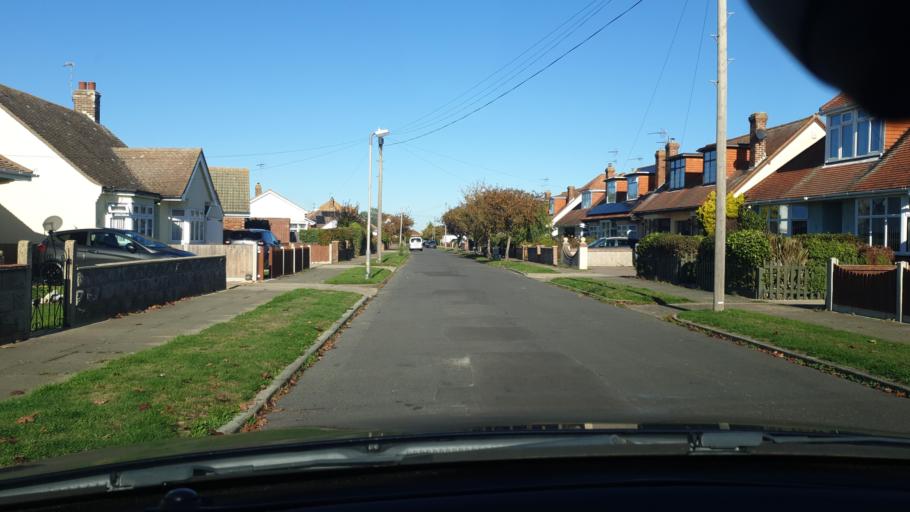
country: GB
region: England
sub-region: Essex
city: Clacton-on-Sea
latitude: 51.8031
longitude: 1.1884
